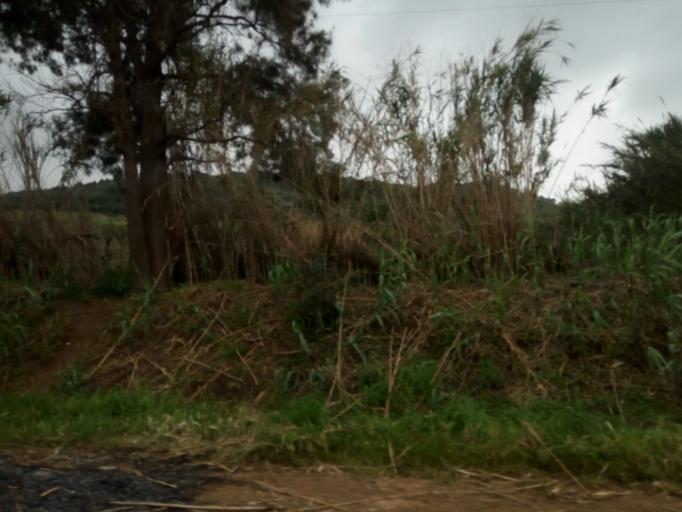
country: DZ
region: Tipaza
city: Tipasa
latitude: 36.5894
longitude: 2.5304
